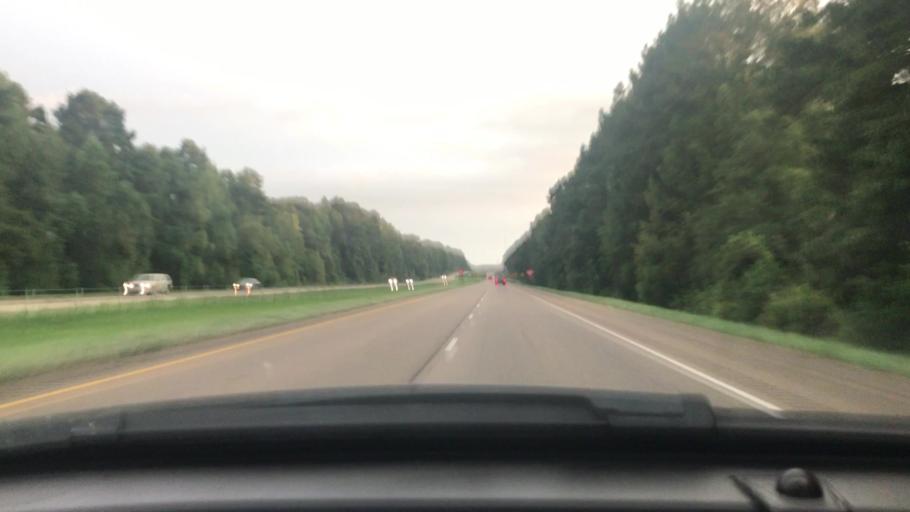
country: US
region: Louisiana
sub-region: Tangipahoa Parish
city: Kentwood
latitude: 30.9698
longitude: -90.5143
